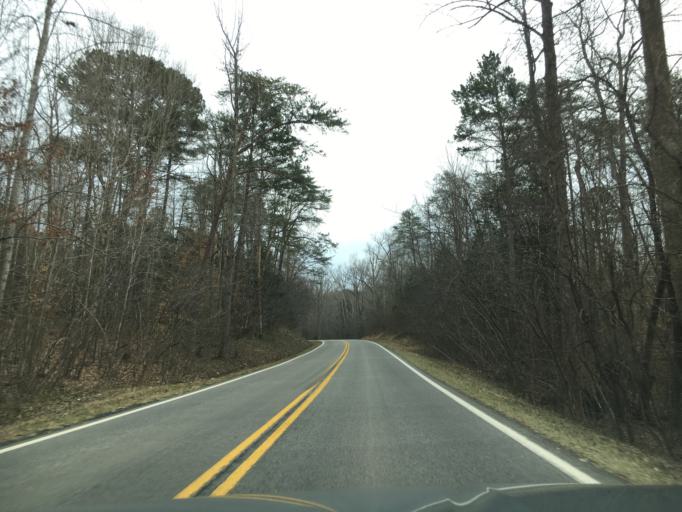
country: US
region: Virginia
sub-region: Charlotte County
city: Charlotte Court House
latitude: 37.1165
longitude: -78.7563
